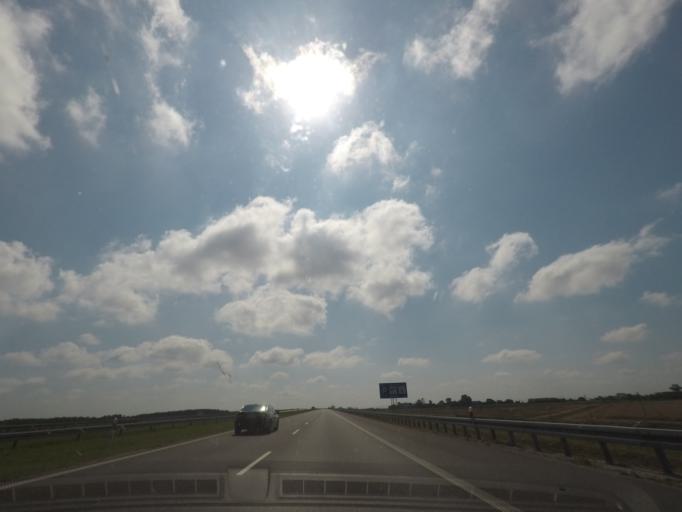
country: PL
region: Kujawsko-Pomorskie
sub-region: Powiat wloclawski
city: Brzesc Kujawski
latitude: 52.6103
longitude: 18.9747
